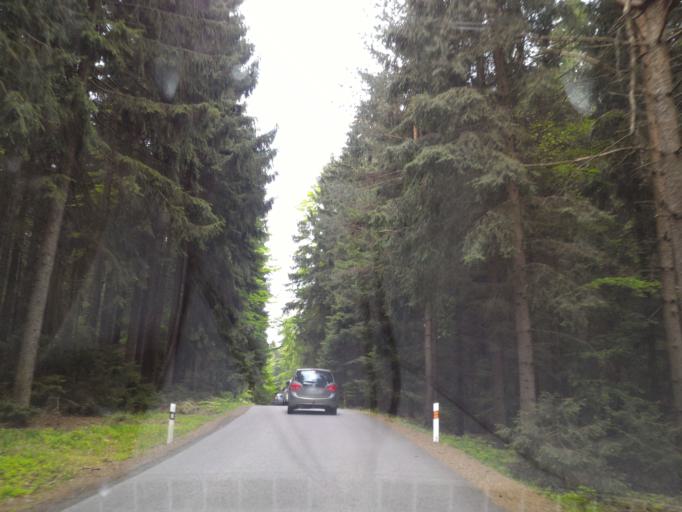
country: CZ
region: Vysocina
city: Ledec nad Sazavou
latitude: 49.6206
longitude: 15.2852
